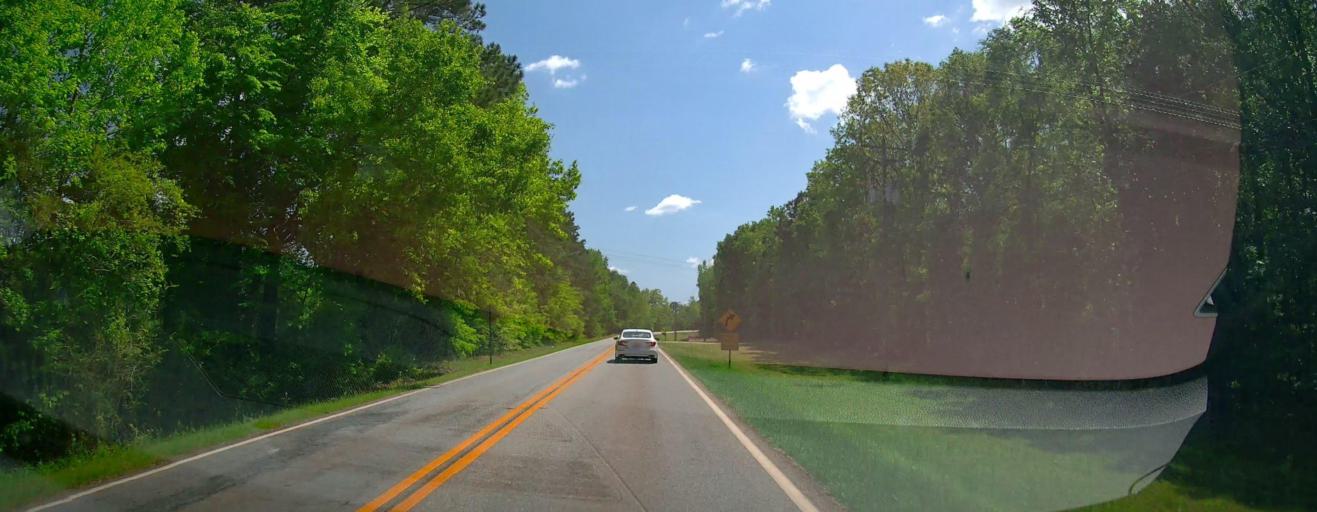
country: US
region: Georgia
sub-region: Putnam County
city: Eatonton
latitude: 33.3100
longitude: -83.3004
